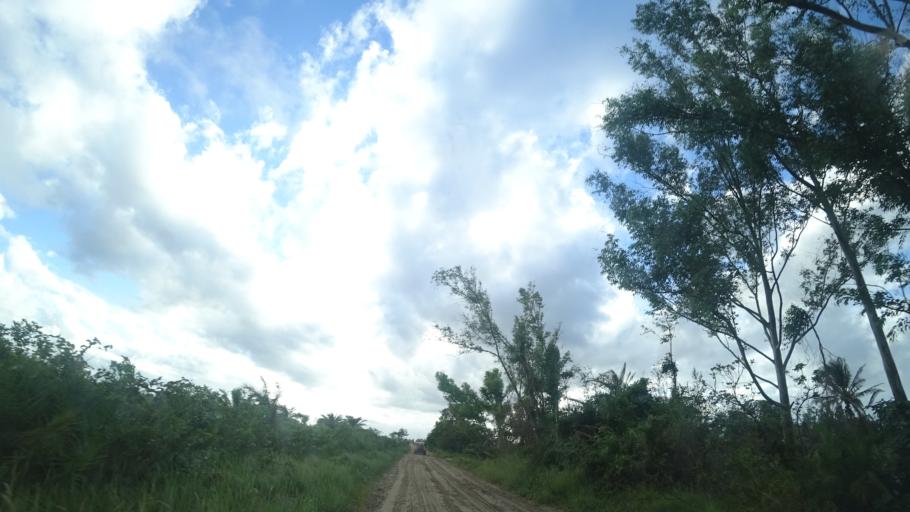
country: MZ
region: Sofala
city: Beira
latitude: -19.7255
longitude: 34.9915
